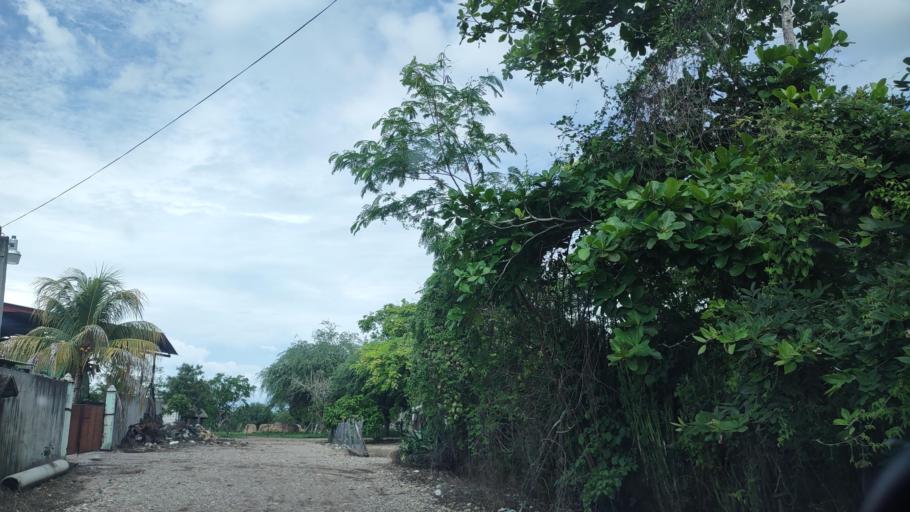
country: MX
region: Veracruz
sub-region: Panuco
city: Oviedo
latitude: 22.0029
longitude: -98.4545
